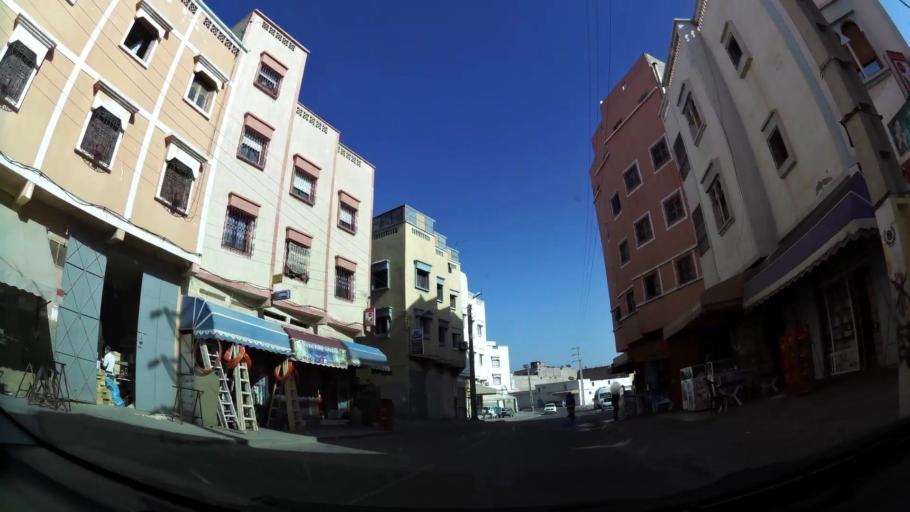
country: MA
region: Souss-Massa-Draa
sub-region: Inezgane-Ait Mellou
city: Inezgane
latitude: 30.3750
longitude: -9.5066
